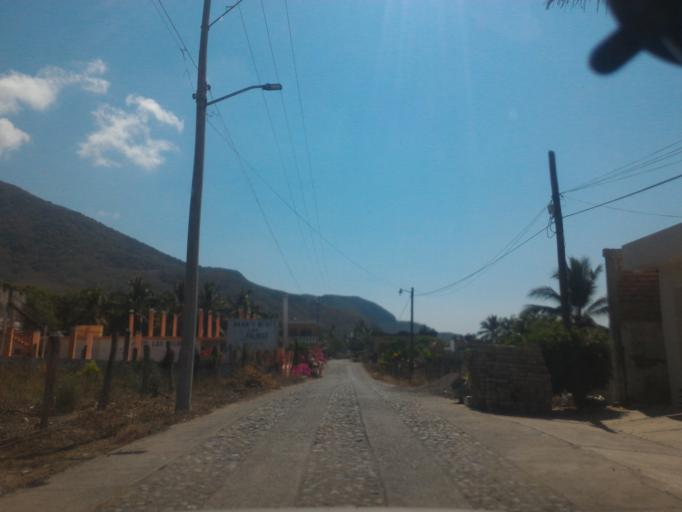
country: MX
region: Michoacan
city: Coahuayana Viejo
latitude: 18.5784
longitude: -103.6672
